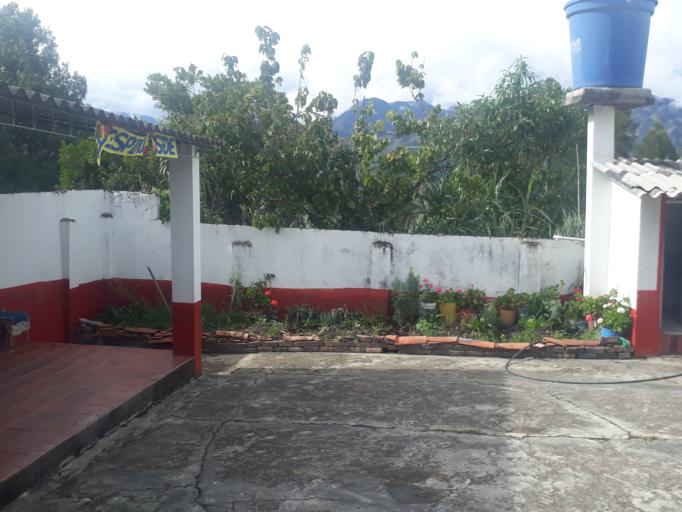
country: CO
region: Boyaca
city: El Espino
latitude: 6.4965
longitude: -72.5023
